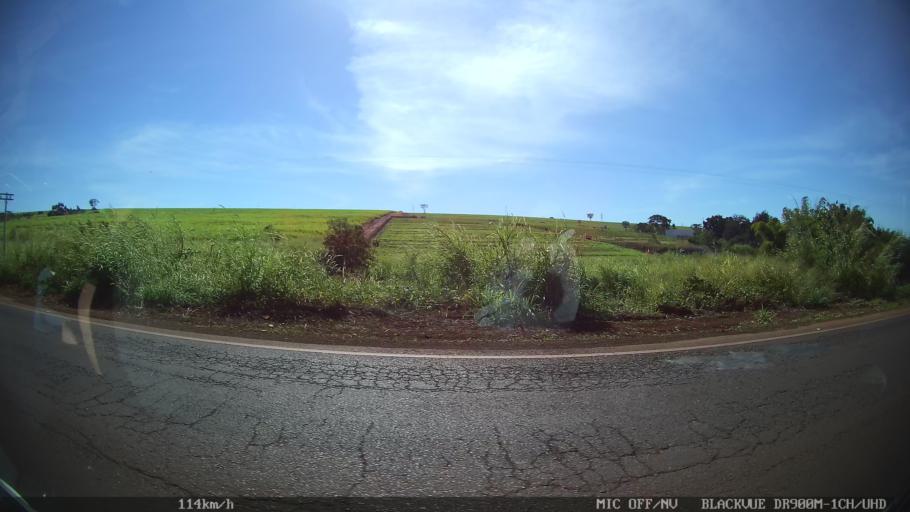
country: BR
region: Sao Paulo
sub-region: Ipua
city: Ipua
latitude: -20.4930
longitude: -48.0179
